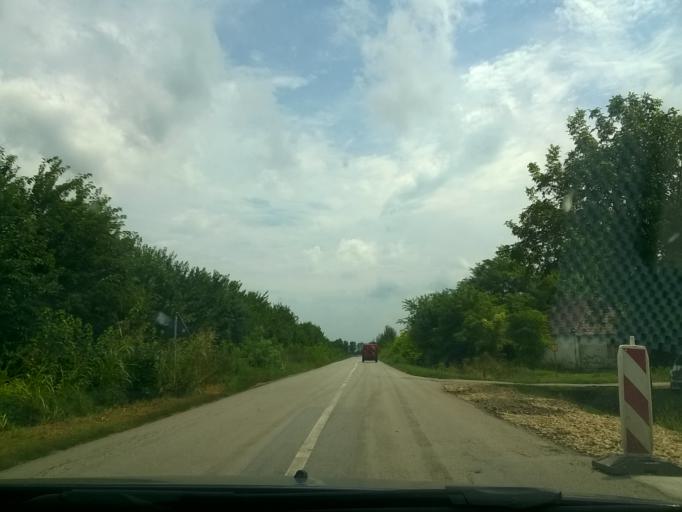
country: RS
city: Hajducica
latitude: 45.2560
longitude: 20.9650
